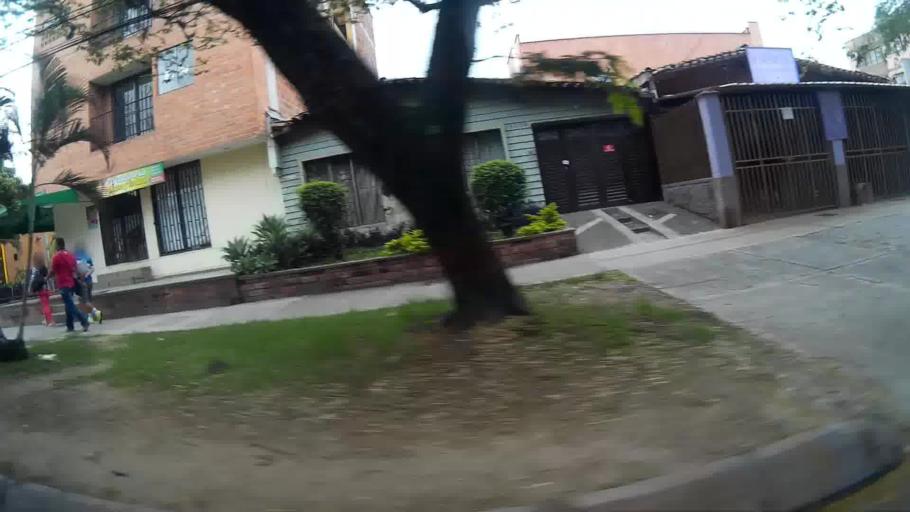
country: CO
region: Antioquia
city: Medellin
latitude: 6.2371
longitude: -75.5874
